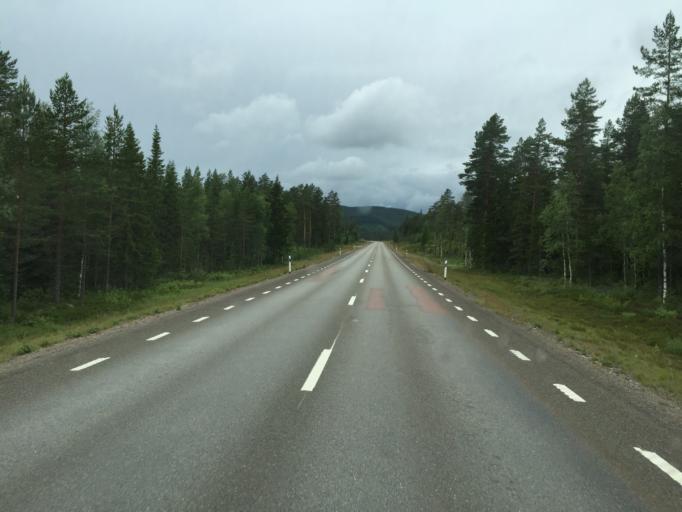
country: SE
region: Dalarna
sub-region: Malung-Saelens kommun
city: Malung
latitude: 60.6489
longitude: 13.6516
